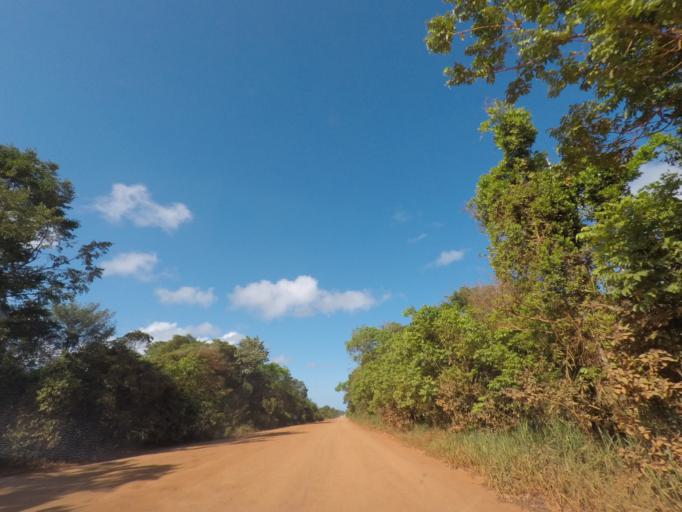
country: BR
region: Bahia
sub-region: Marau
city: Marau
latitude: -14.1553
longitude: -39.0088
